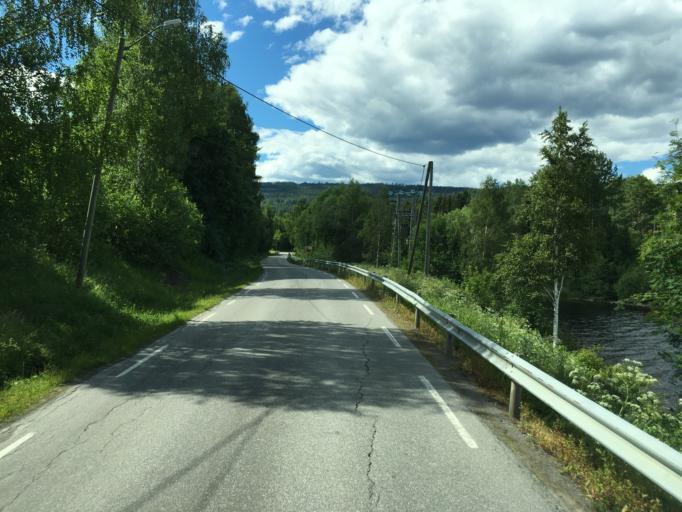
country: NO
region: Oppland
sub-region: Sondre Land
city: Hov
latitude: 60.5188
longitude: 10.2921
